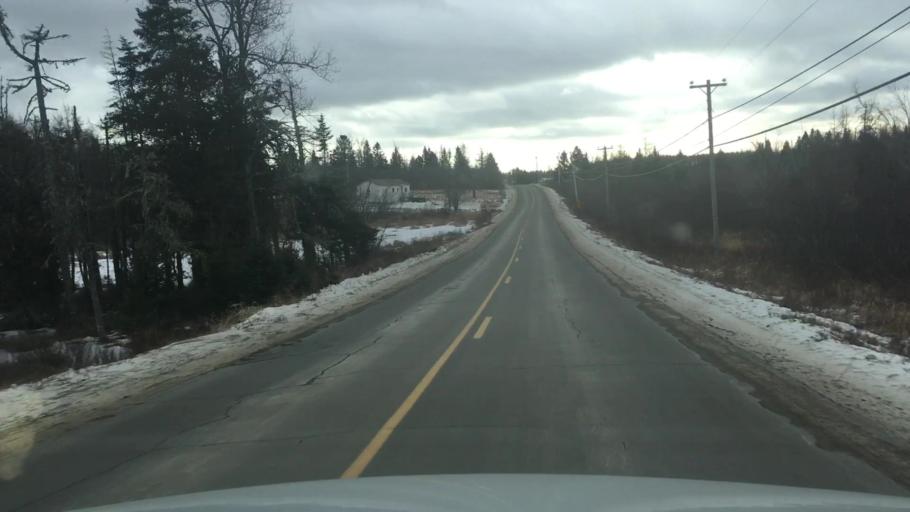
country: US
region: Maine
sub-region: Washington County
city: Machias
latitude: 44.6832
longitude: -67.4671
